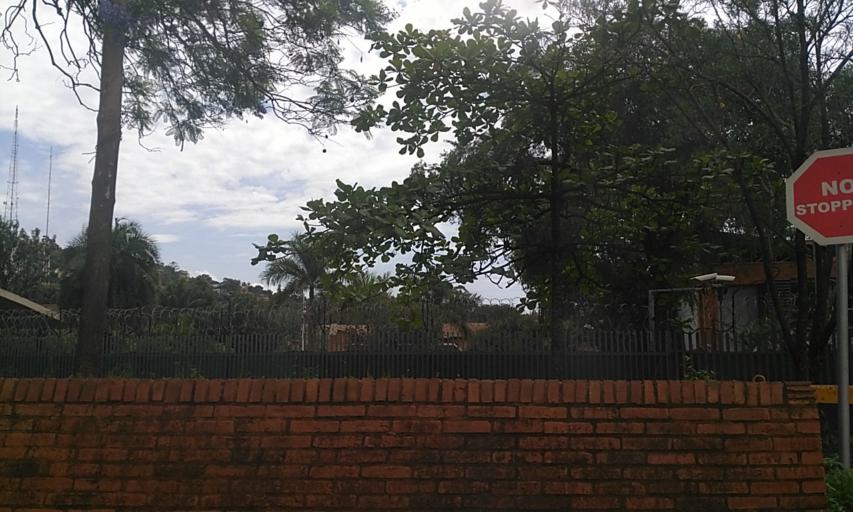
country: UG
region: Central Region
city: Kampala Central Division
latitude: 0.3373
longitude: 32.5841
